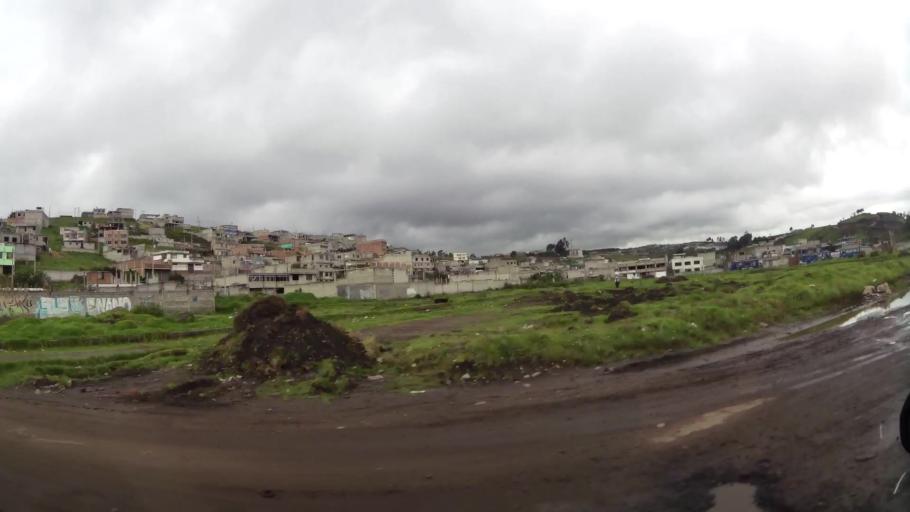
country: EC
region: Pichincha
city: Sangolqui
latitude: -0.3155
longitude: -78.5286
